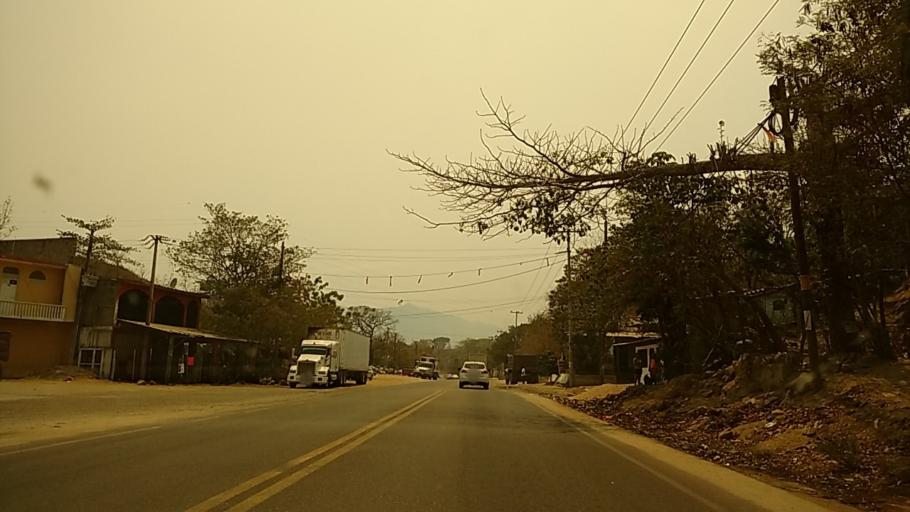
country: MX
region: Guerrero
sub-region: Acapulco de Juarez
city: Colonia Nueva Revolucion
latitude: 16.9415
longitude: -99.8136
